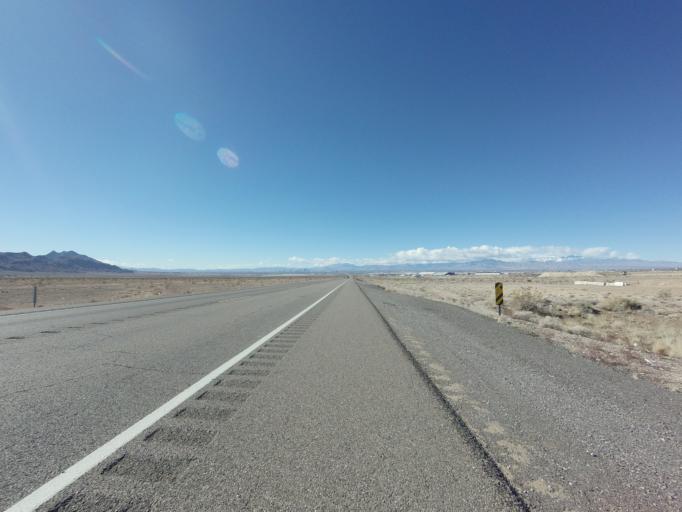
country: US
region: Nevada
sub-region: Clark County
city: Nellis Air Force Base
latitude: 36.2832
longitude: -114.9814
